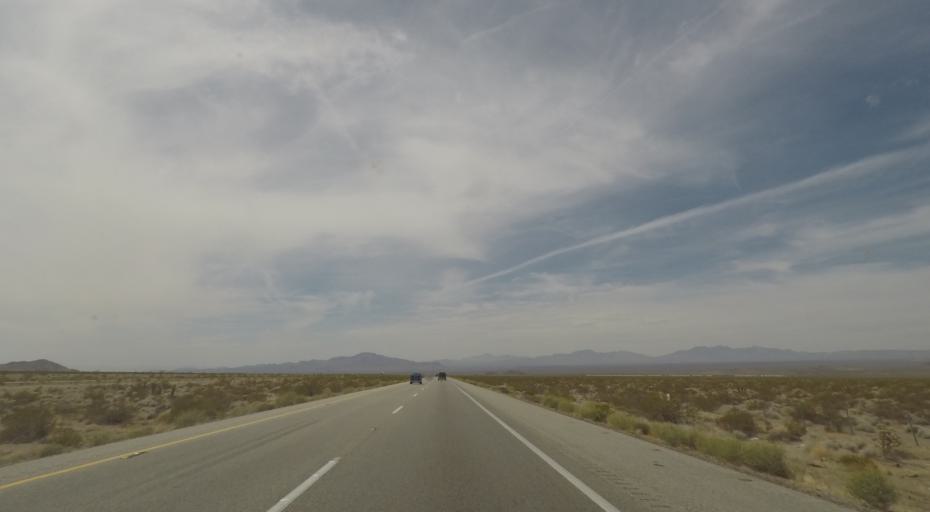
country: US
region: California
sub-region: San Bernardino County
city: Needles
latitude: 34.8224
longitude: -115.1111
